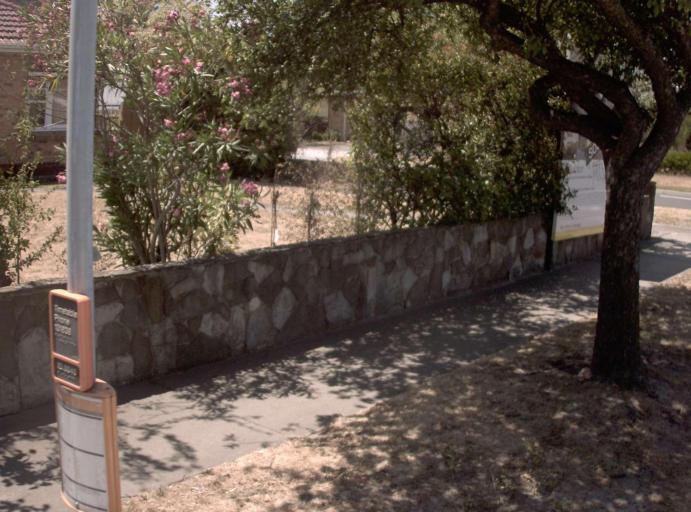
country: AU
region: Victoria
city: Hughesdale
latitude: -37.9098
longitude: 145.0880
